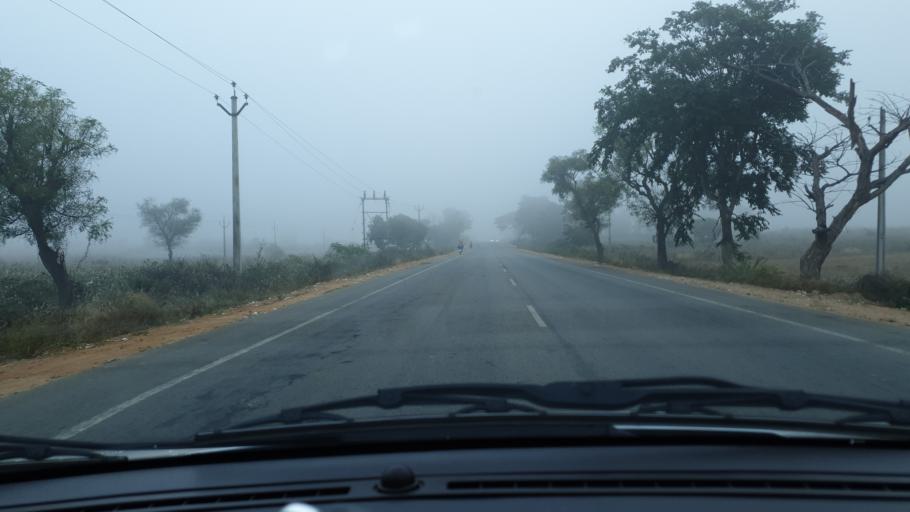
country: IN
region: Telangana
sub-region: Mahbubnagar
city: Nagar Karnul
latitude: 16.6635
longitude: 78.5673
